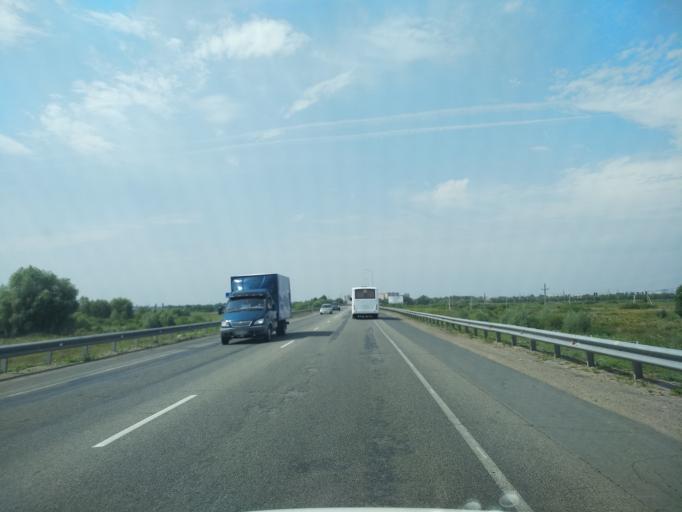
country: RU
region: Voronezj
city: Somovo
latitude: 51.6863
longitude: 39.3537
